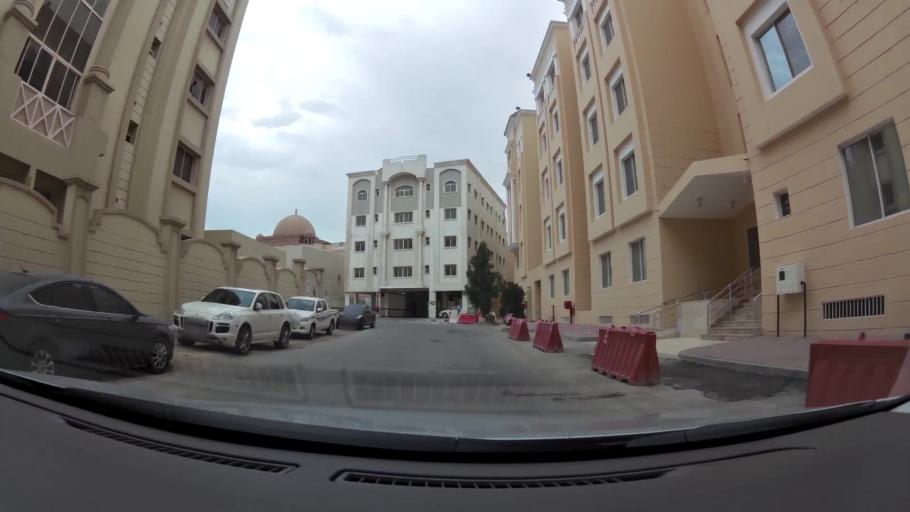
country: QA
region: Baladiyat ad Dawhah
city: Doha
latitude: 25.2747
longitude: 51.5005
